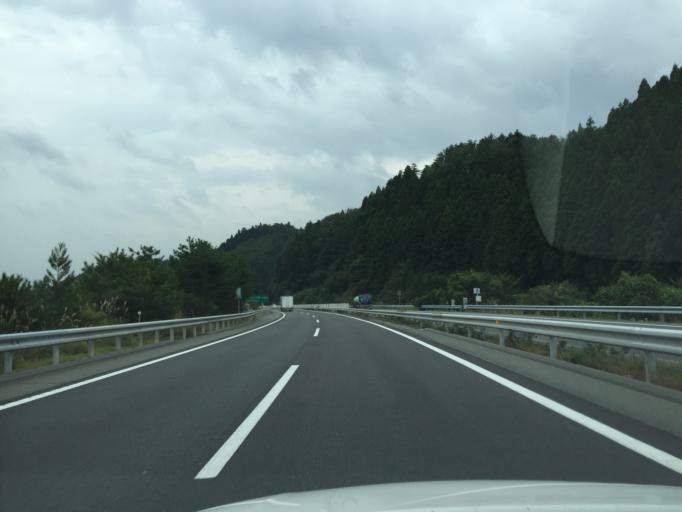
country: JP
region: Fukushima
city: Iwaki
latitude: 37.1145
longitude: 140.7522
